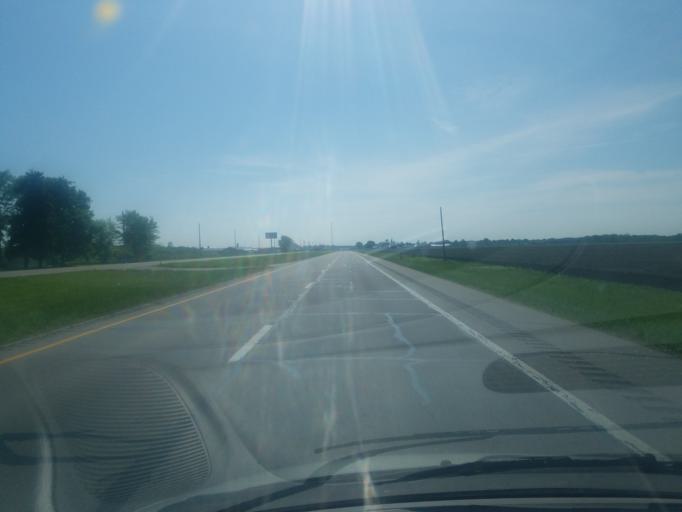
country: US
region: Ohio
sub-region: Huron County
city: Monroeville
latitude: 41.2536
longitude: -82.7306
